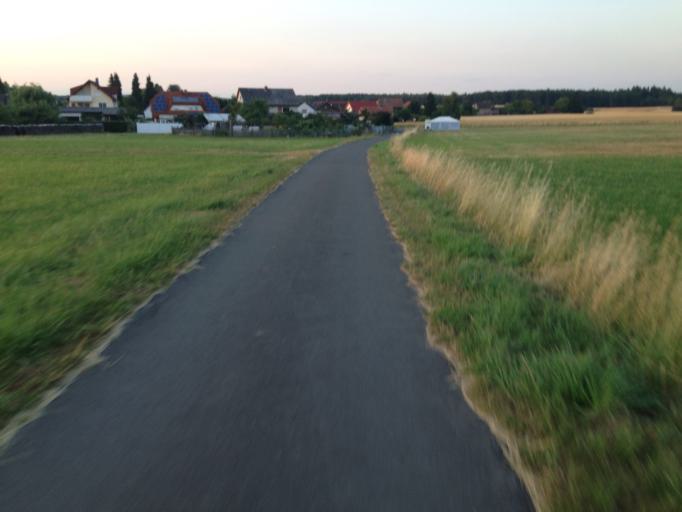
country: DE
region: Hesse
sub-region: Regierungsbezirk Giessen
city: Grossen Buseck
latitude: 50.5724
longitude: 8.7531
